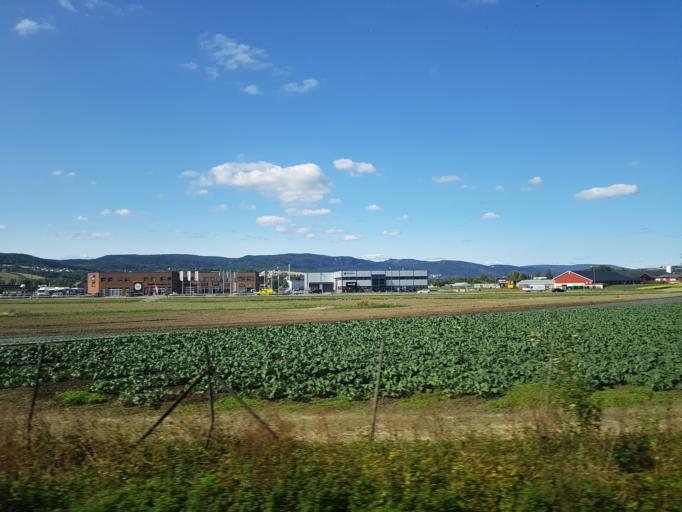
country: NO
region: Buskerud
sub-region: Lier
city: Lierbyen
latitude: 59.7572
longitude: 10.2727
